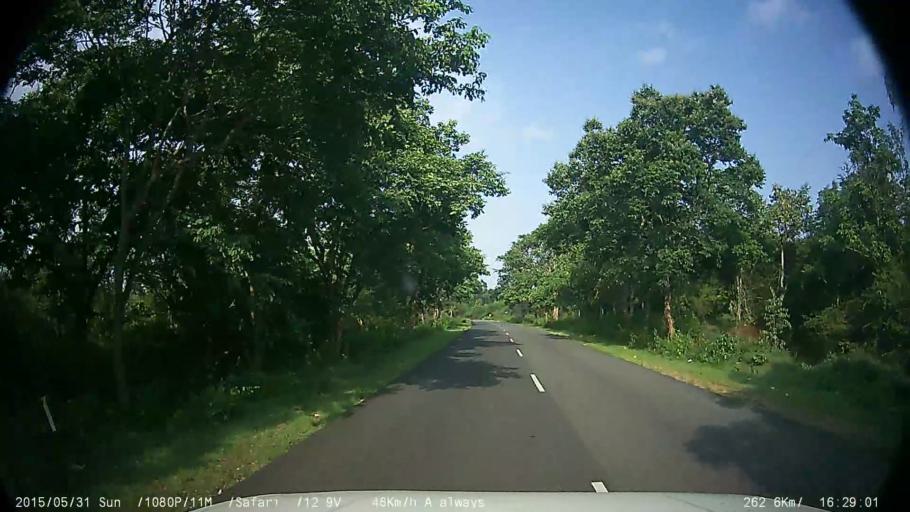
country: IN
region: Karnataka
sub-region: Chamrajnagar
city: Gundlupet
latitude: 11.7692
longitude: 76.5448
